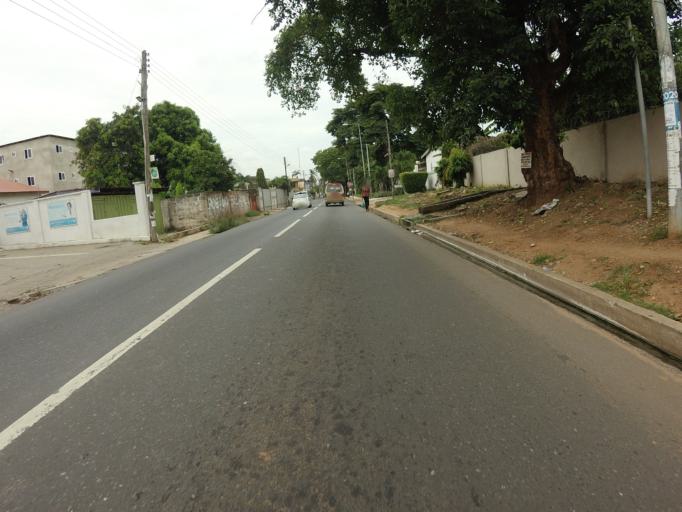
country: GH
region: Greater Accra
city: Dome
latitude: 5.5990
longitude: -0.2271
